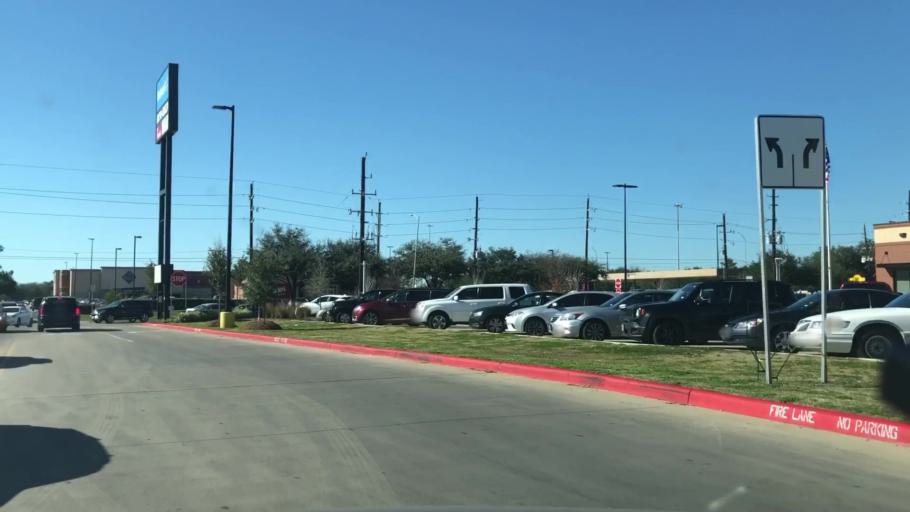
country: US
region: Texas
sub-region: Harris County
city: Bellaire
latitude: 29.7238
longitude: -95.4674
